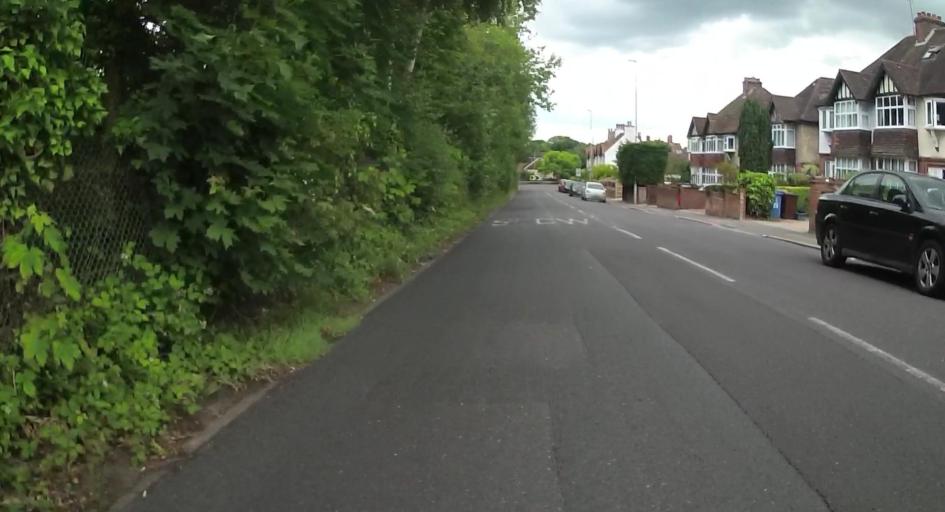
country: GB
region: England
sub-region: Hampshire
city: Aldershot
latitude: 51.2391
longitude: -0.7668
